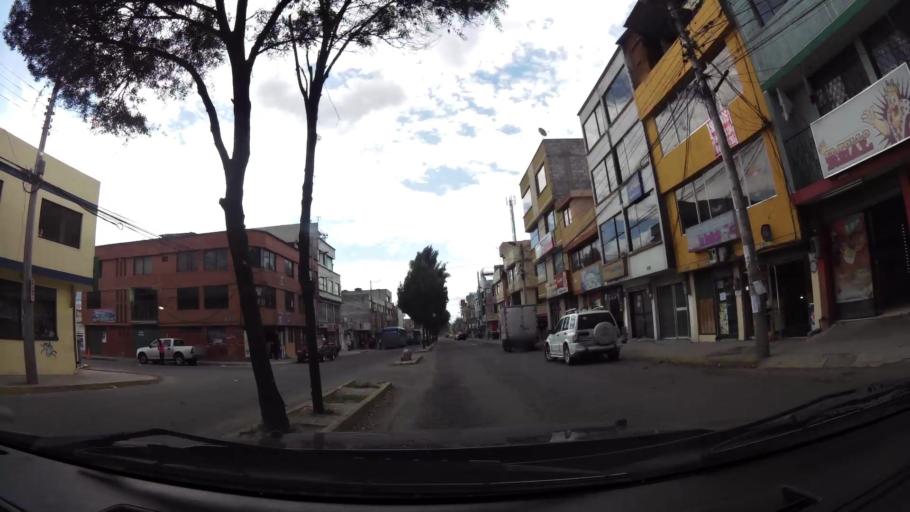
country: EC
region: Pichincha
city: Quito
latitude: -0.1011
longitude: -78.4536
